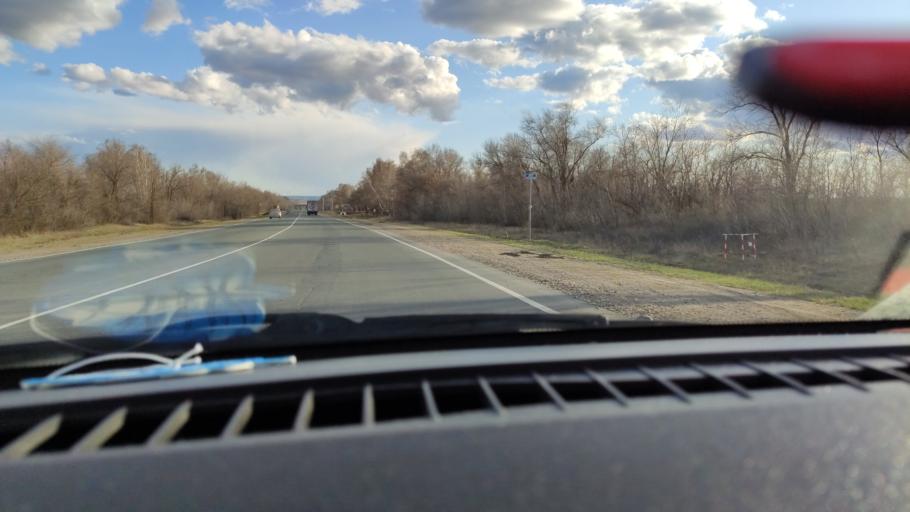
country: RU
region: Saratov
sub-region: Saratovskiy Rayon
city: Saratov
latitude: 51.7032
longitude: 46.0125
